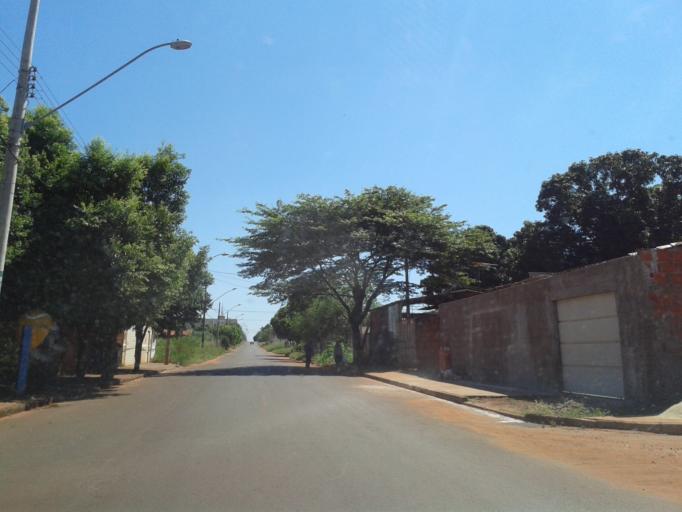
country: BR
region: Minas Gerais
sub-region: Ituiutaba
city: Ituiutaba
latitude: -18.9997
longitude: -49.4546
